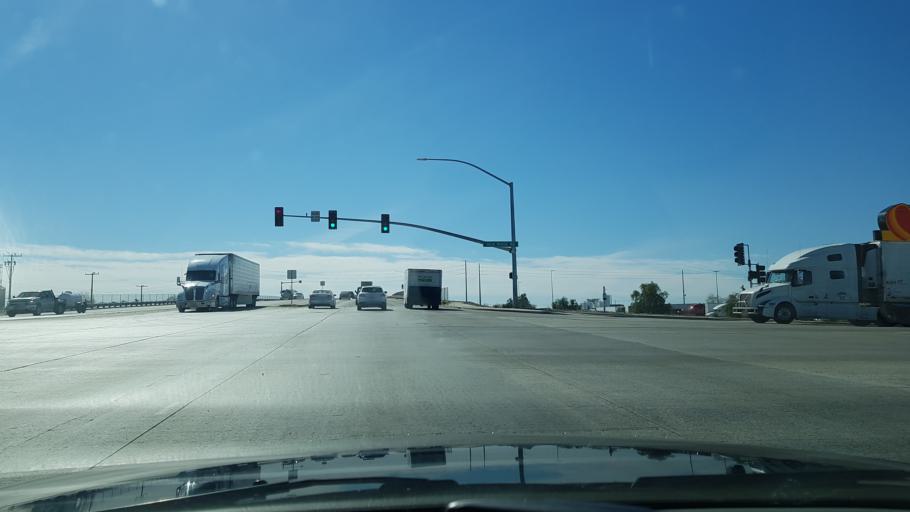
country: US
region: Arizona
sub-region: Yuma County
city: Yuma
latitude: 32.6873
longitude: -114.5817
